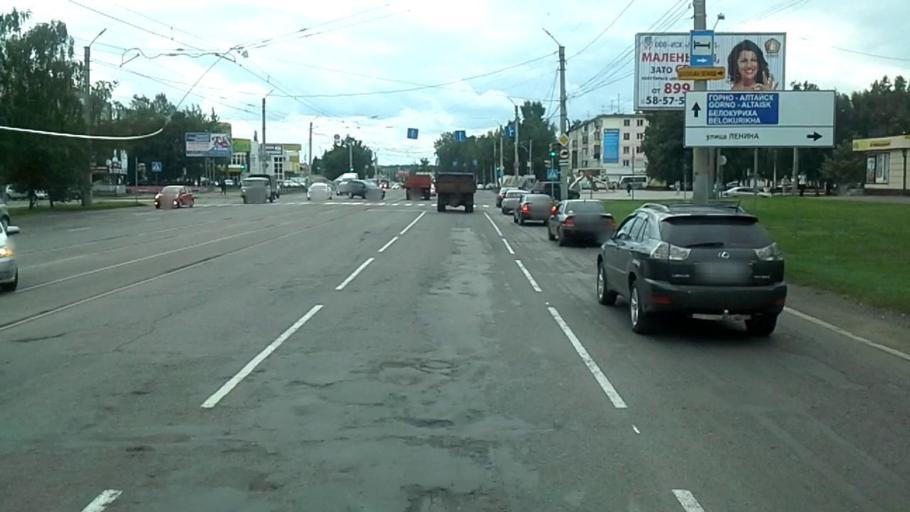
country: RU
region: Altai Krai
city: Biysk
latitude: 52.5423
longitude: 85.2187
